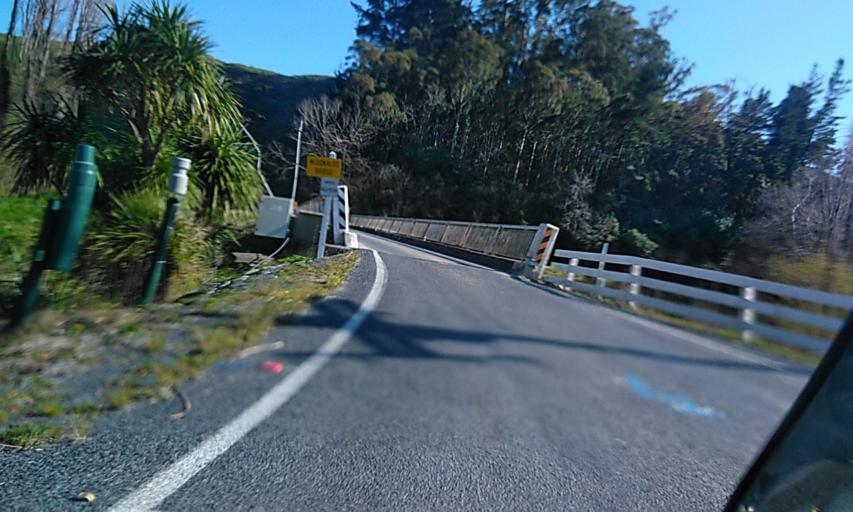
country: NZ
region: Gisborne
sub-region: Gisborne District
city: Gisborne
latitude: -38.5145
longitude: 178.0404
